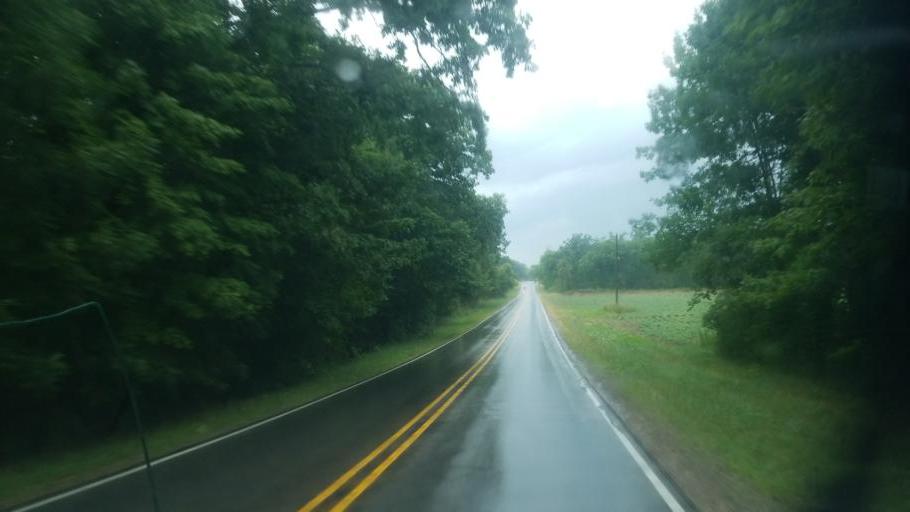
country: US
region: Indiana
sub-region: Steuben County
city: Hamilton
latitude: 41.5094
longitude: -84.8729
